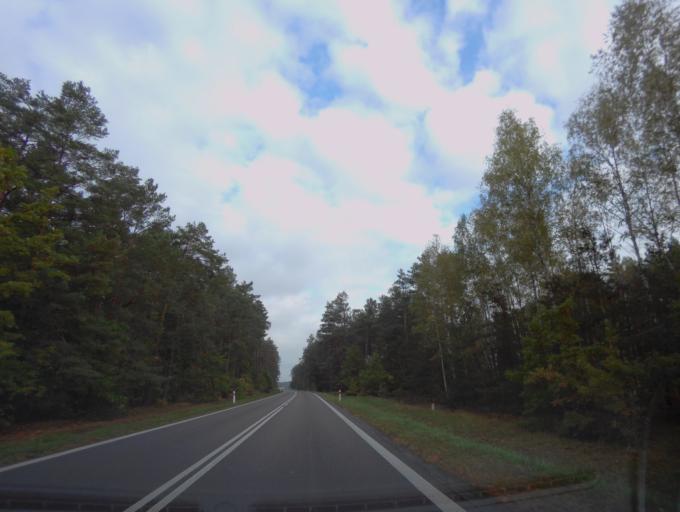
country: PL
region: Lublin Voivodeship
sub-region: Powiat bilgorajski
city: Frampol
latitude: 50.6014
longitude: 22.6786
